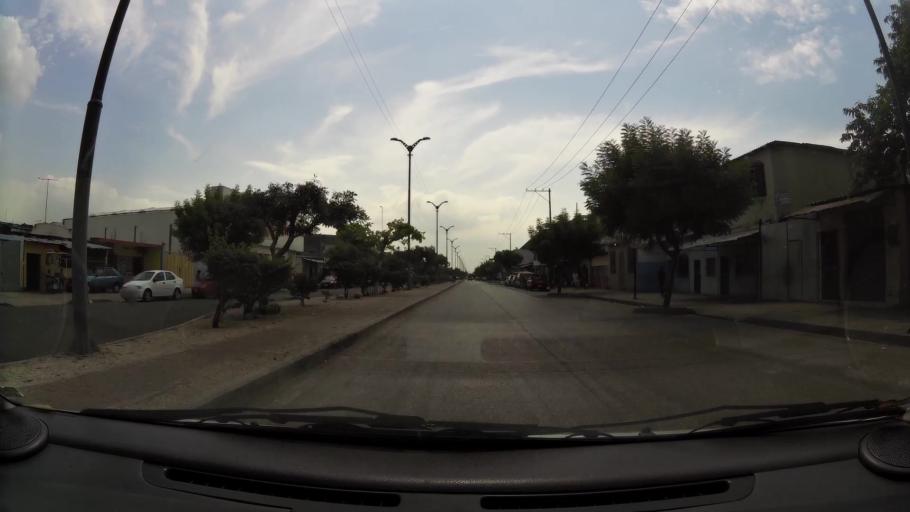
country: EC
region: Guayas
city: Guayaquil
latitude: -2.2830
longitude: -79.8838
